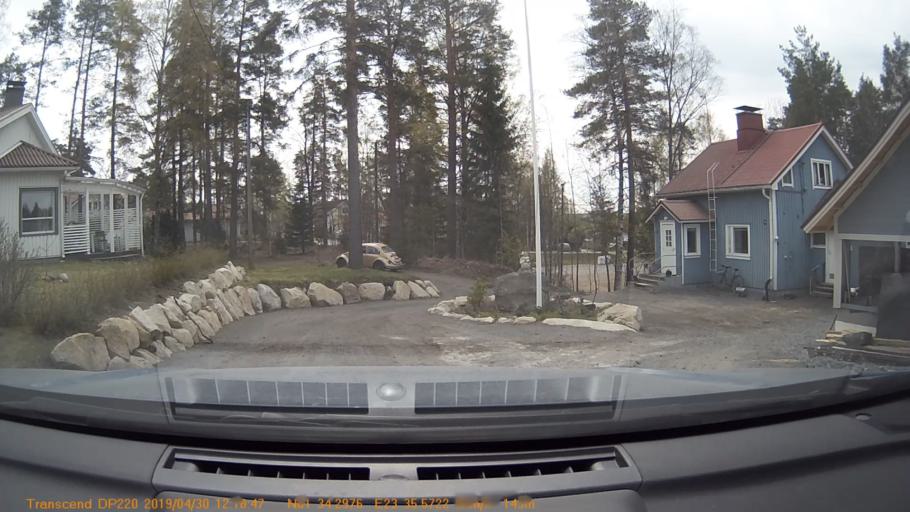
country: FI
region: Pirkanmaa
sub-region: Tampere
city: Yloejaervi
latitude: 61.5717
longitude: 23.5928
